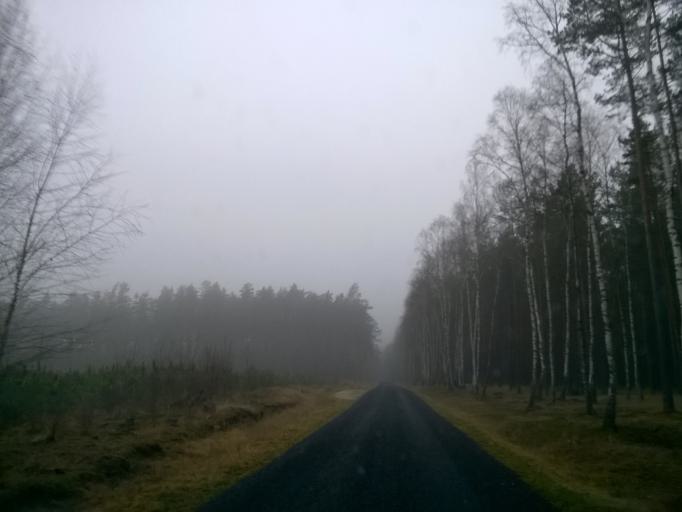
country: PL
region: Kujawsko-Pomorskie
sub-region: Powiat nakielski
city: Kcynia
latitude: 53.0438
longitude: 17.5210
